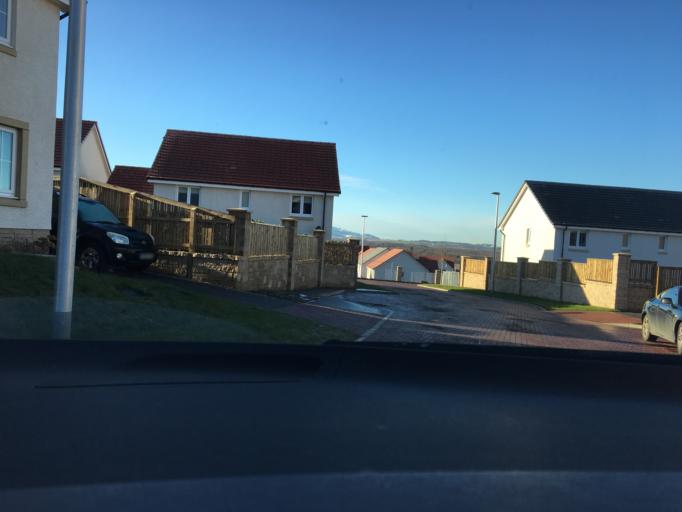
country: GB
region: Scotland
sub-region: Midlothian
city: Dalkeith
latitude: 55.8987
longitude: -3.0364
